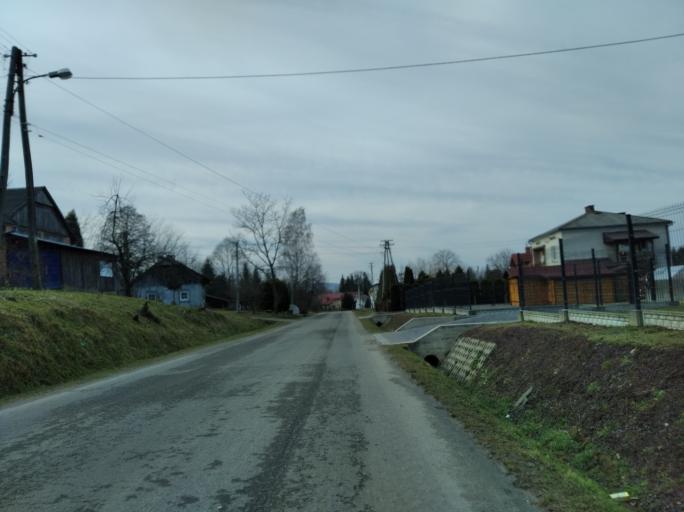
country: PL
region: Subcarpathian Voivodeship
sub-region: Powiat brzozowski
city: Gorki
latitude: 49.6431
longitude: 22.0441
